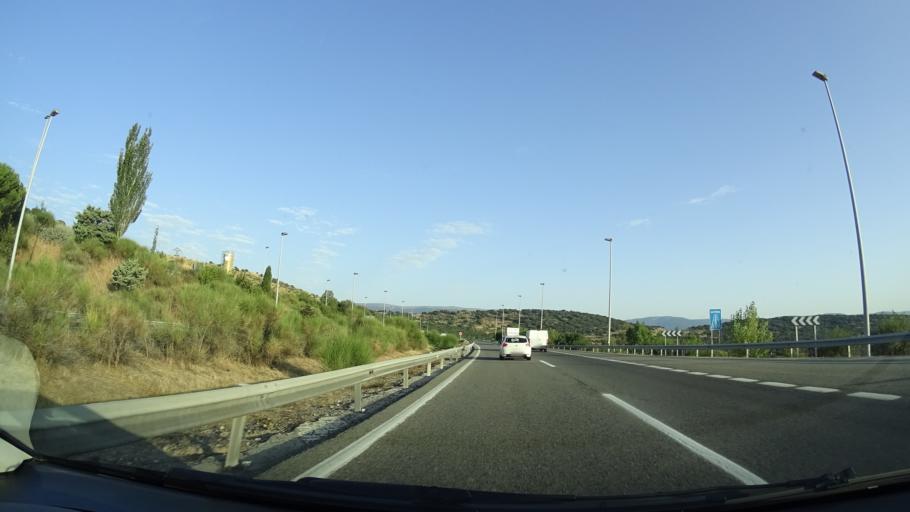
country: ES
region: Madrid
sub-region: Provincia de Madrid
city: Buitrago del Lozoya
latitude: 40.9428
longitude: -3.6329
